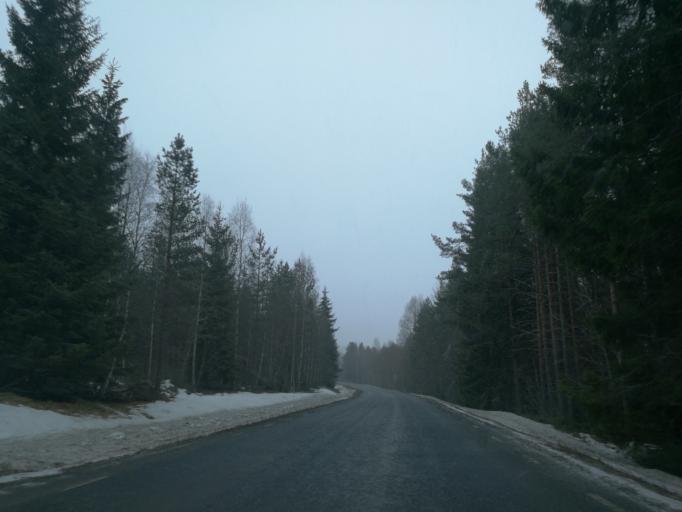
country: NO
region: Hedmark
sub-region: Grue
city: Kirkenaer
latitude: 60.6937
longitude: 12.6253
